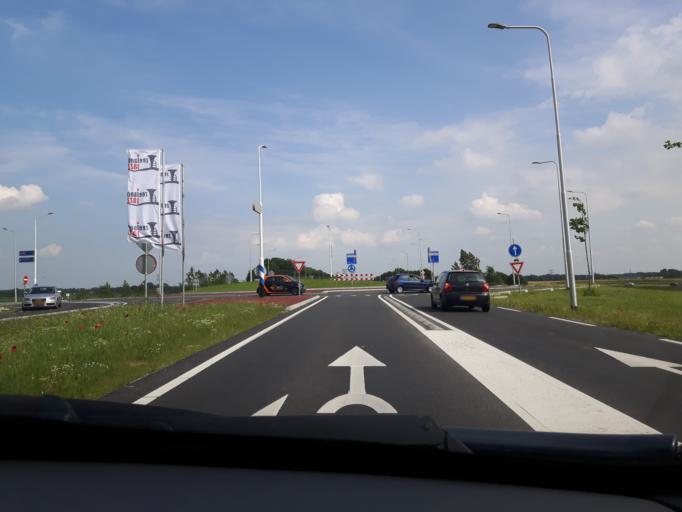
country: NL
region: Zeeland
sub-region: Gemeente Middelburg
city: Middelburg
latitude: 51.4780
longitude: 3.6336
